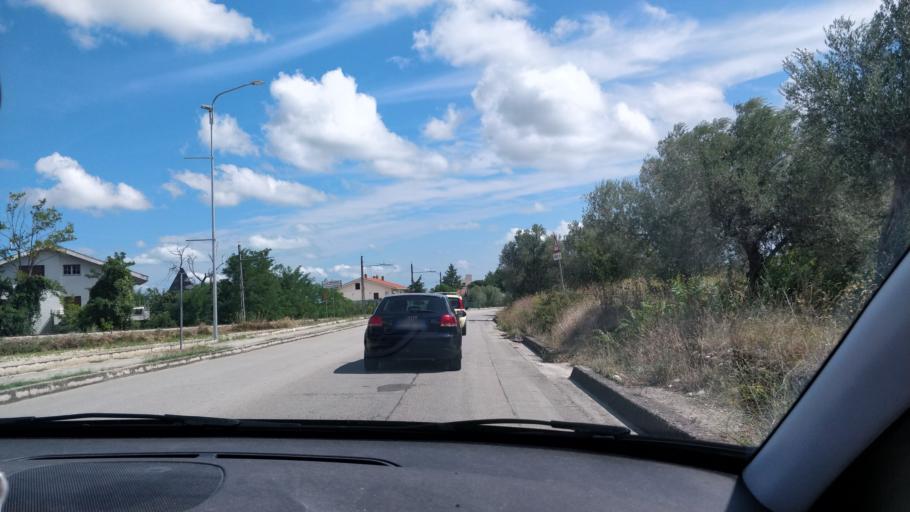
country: IT
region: Abruzzo
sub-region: Provincia di Chieti
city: Treglio
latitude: 42.2479
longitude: 14.4200
